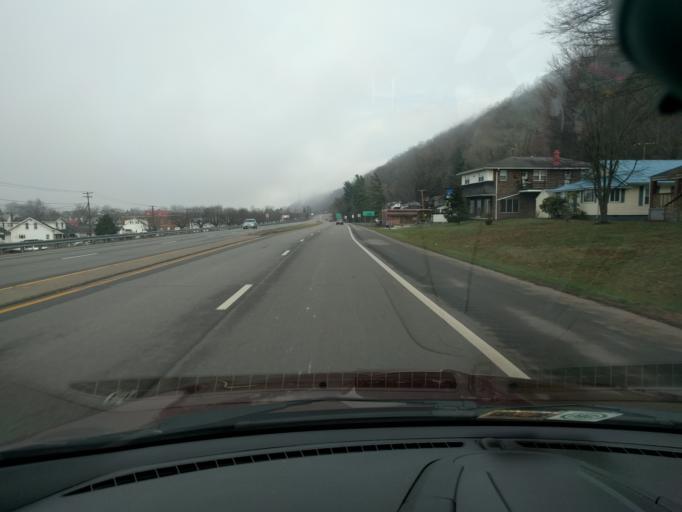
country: US
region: West Virginia
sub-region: Kanawha County
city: Belle
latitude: 38.2303
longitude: -81.5348
